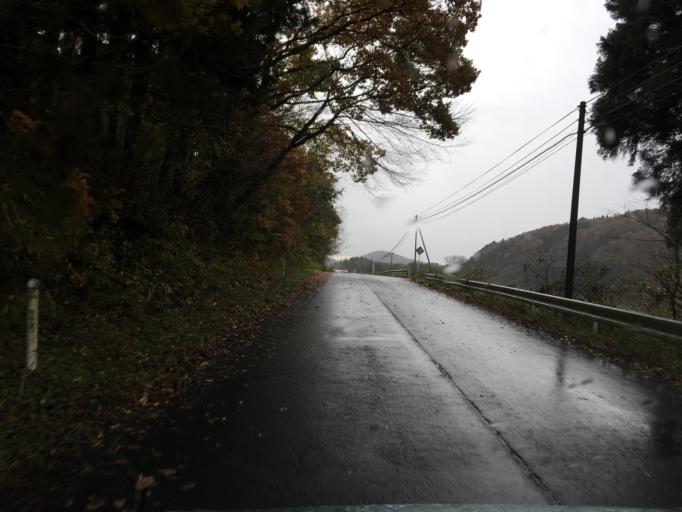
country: JP
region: Iwate
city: Ichinoseki
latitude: 38.8062
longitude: 141.2501
